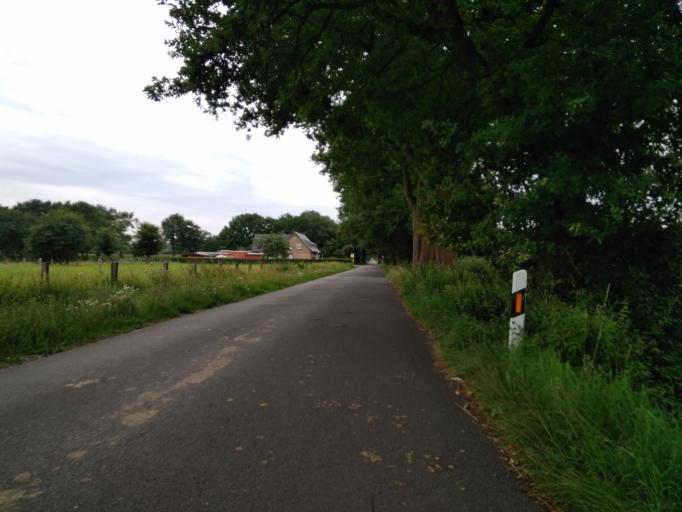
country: DE
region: North Rhine-Westphalia
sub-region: Regierungsbezirk Munster
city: Bottrop
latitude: 51.5946
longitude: 6.8945
